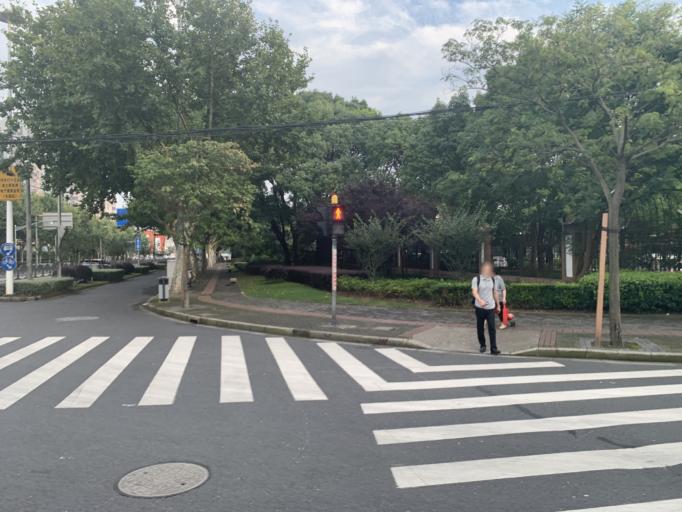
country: CN
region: Shanghai Shi
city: Huamu
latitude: 31.2462
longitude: 121.5714
